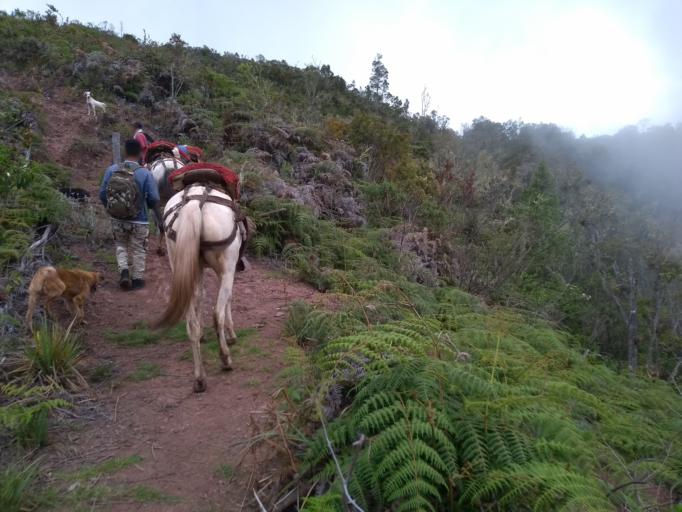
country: CO
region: Cesar
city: Manaure Balcon del Cesar
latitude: 10.2146
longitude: -73.0131
